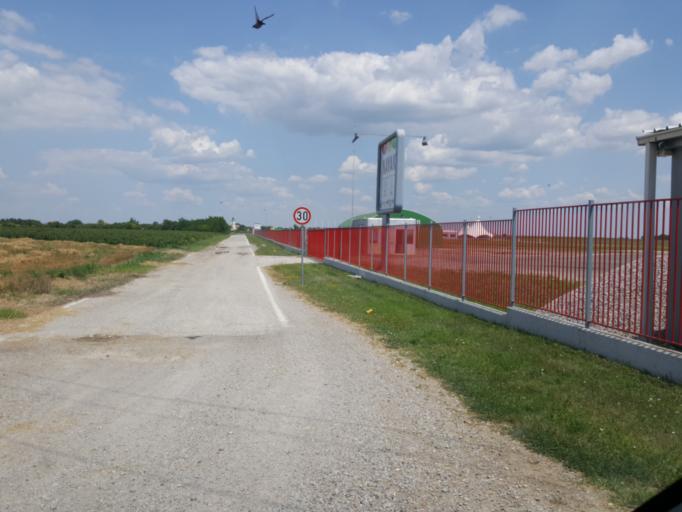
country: RS
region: Autonomna Pokrajina Vojvodina
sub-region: Sremski Okrug
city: Pecinci
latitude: 44.8381
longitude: 19.9482
